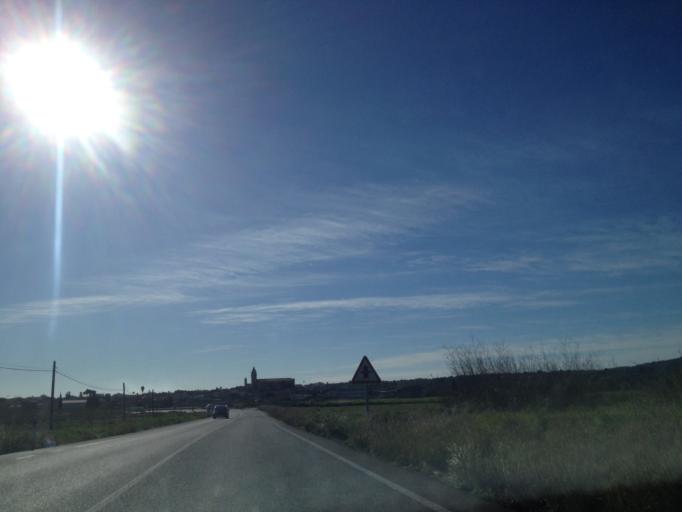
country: ES
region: Balearic Islands
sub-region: Illes Balears
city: Petra
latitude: 39.6237
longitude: 3.1098
